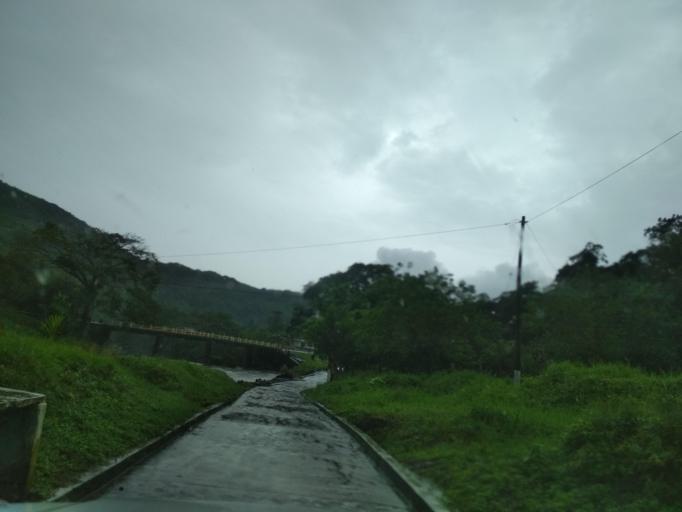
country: MX
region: Veracruz
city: Santiago Tuxtla
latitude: 18.4485
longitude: -95.3176
